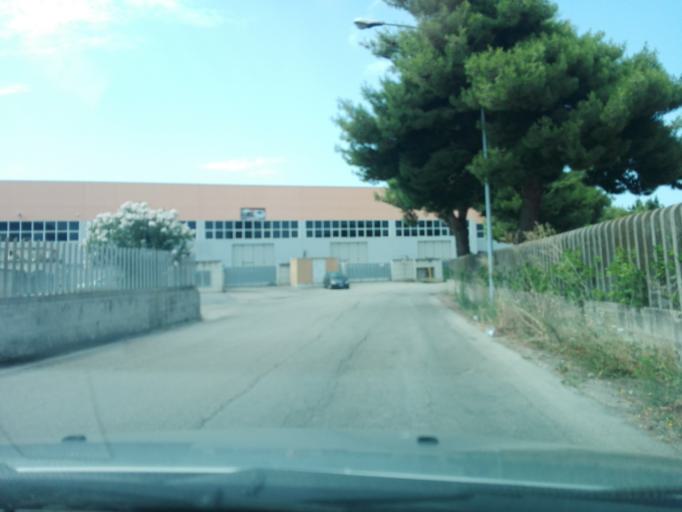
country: IT
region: Abruzzo
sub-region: Provincia di Pescara
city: Montesilvano Marina
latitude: 42.5055
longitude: 14.1296
